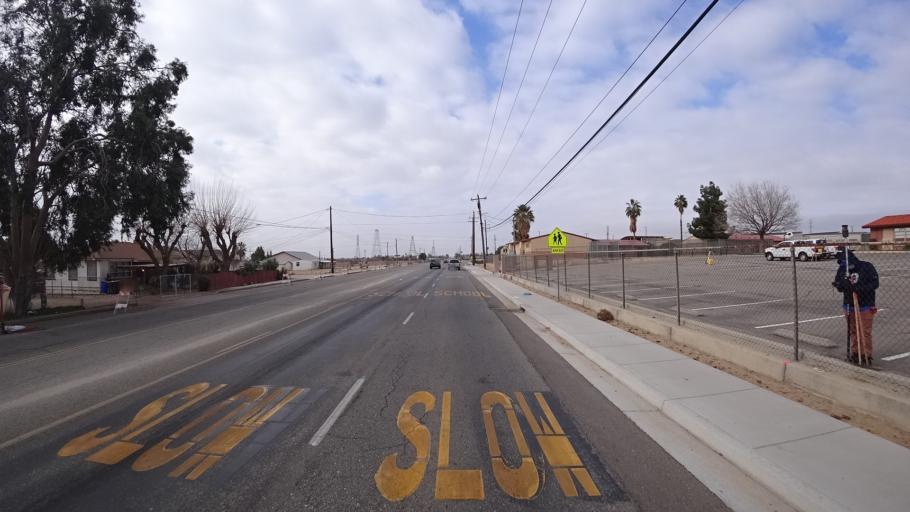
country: US
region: California
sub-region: Kern County
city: Bakersfield
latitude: 35.3763
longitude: -118.9164
